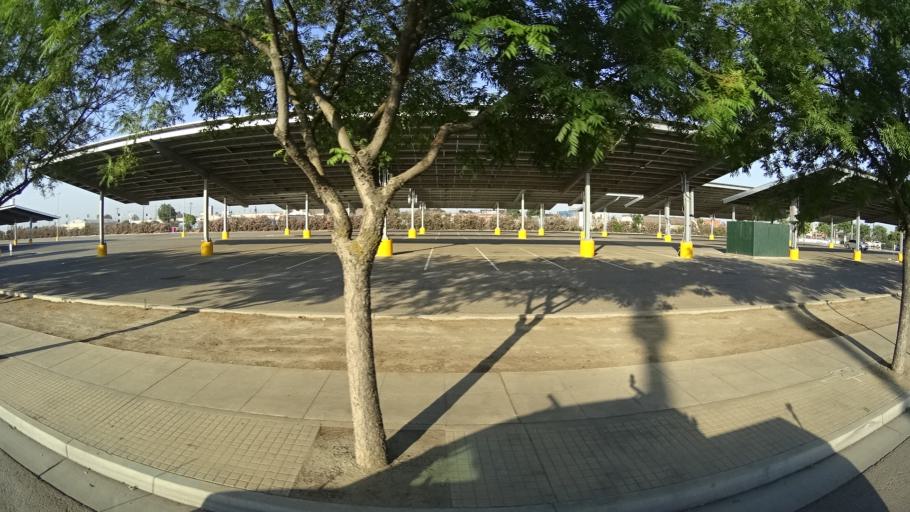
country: US
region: California
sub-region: Fresno County
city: Fresno
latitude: 36.7307
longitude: -119.7905
